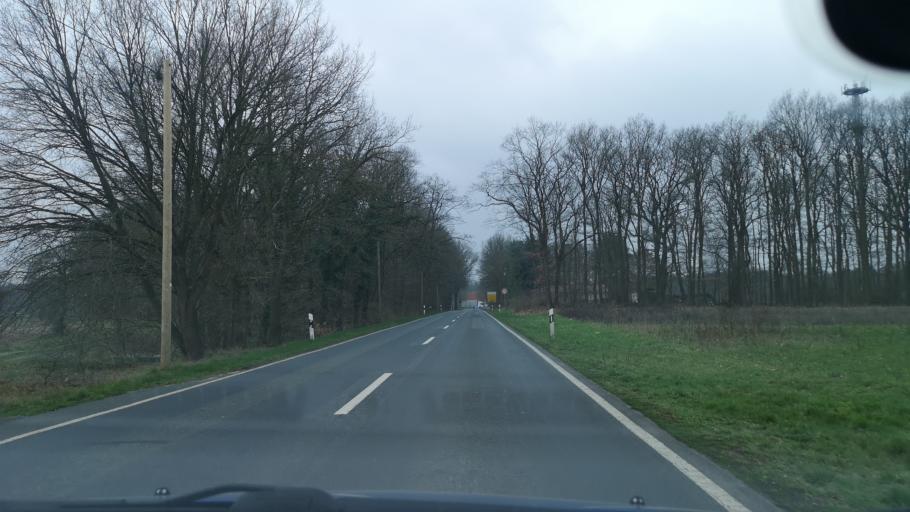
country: DE
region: Lower Saxony
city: Neustadt am Rubenberge
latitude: 52.5394
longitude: 9.4014
